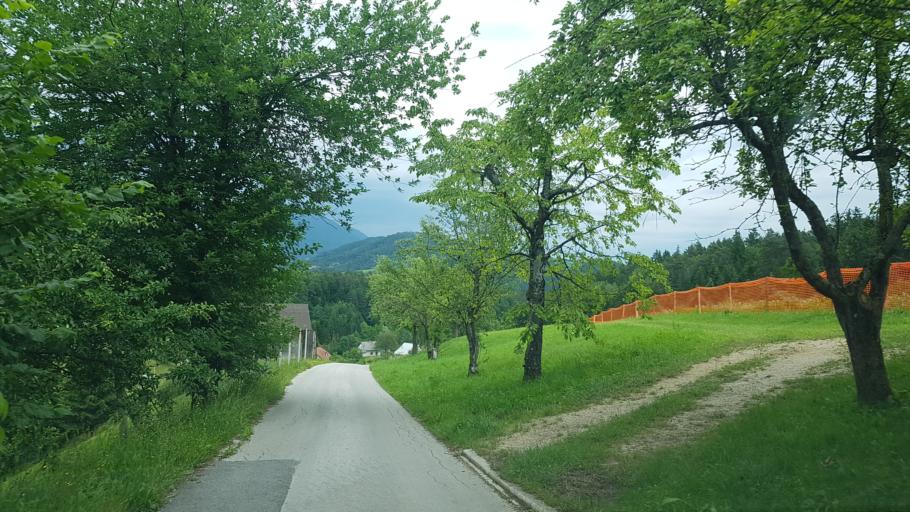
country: SI
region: Dobrna
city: Dobrna
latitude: 46.3439
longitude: 15.2580
